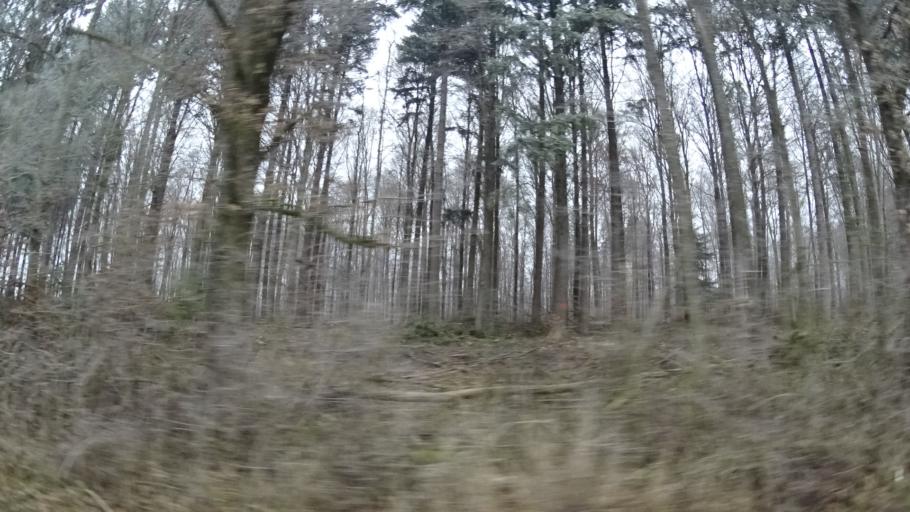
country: DE
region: Baden-Wuerttemberg
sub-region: Karlsruhe Region
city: Seckach
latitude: 49.4702
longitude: 9.3481
